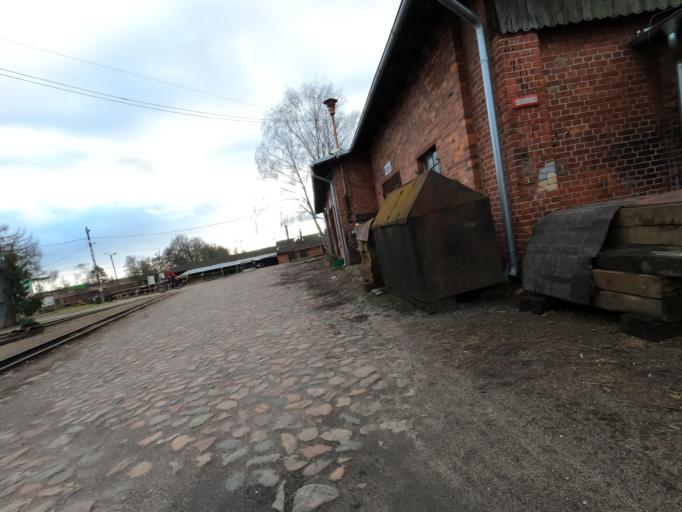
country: PL
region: Greater Poland Voivodeship
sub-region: Powiat pilski
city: Bialosliwie
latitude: 53.0972
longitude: 17.1171
